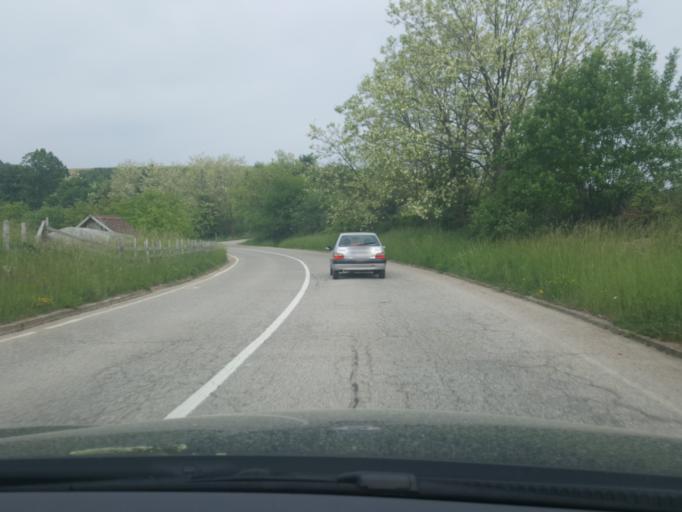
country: RS
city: Kamenica
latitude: 44.2452
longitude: 19.7339
